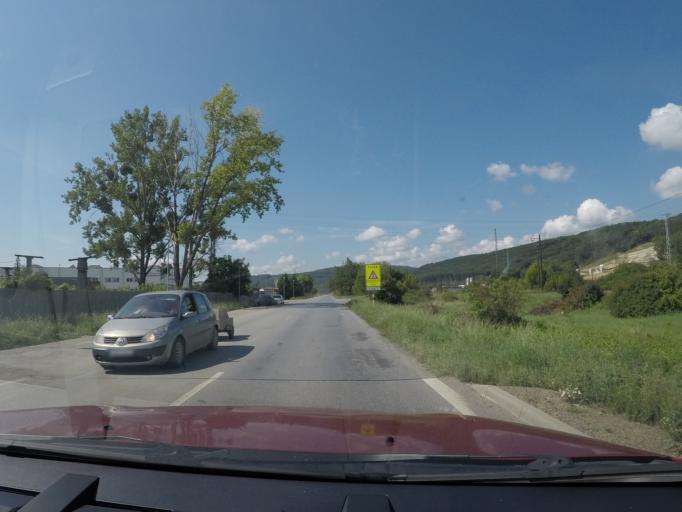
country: SK
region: Presovsky
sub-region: Okres Presov
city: Presov
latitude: 48.9679
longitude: 21.2505
